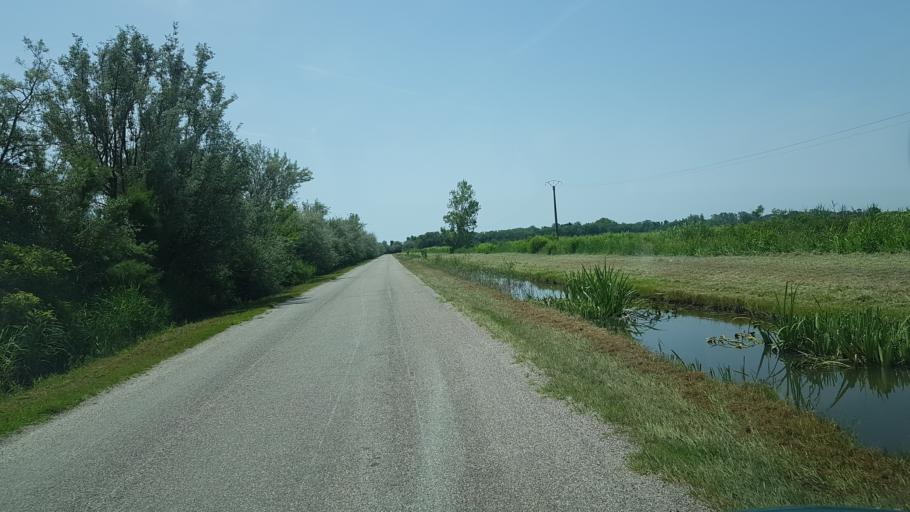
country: FR
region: Languedoc-Roussillon
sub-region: Departement du Gard
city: Saint-Gilles
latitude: 43.5796
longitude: 4.5040
